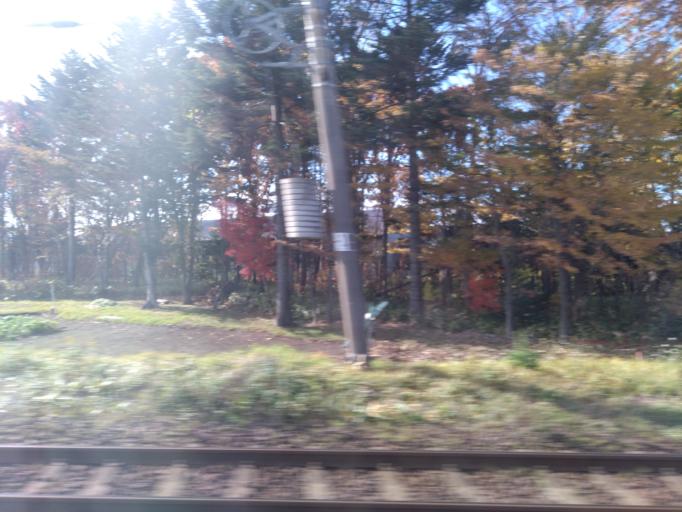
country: JP
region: Hokkaido
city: Kitahiroshima
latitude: 42.9248
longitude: 141.5730
